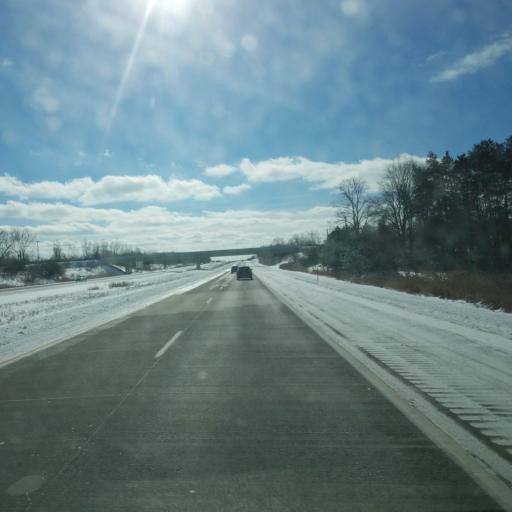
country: US
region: Michigan
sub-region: Clinton County
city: DeWitt
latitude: 42.9093
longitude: -84.5178
